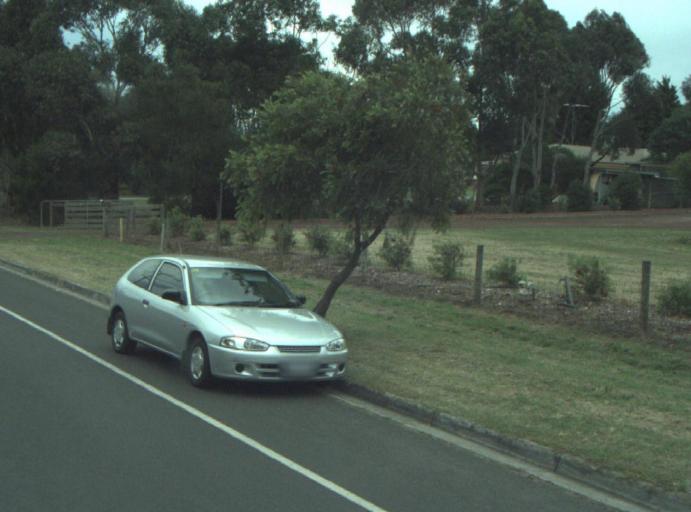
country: AU
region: Victoria
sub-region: Greater Geelong
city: Leopold
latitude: -38.1959
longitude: 144.4676
